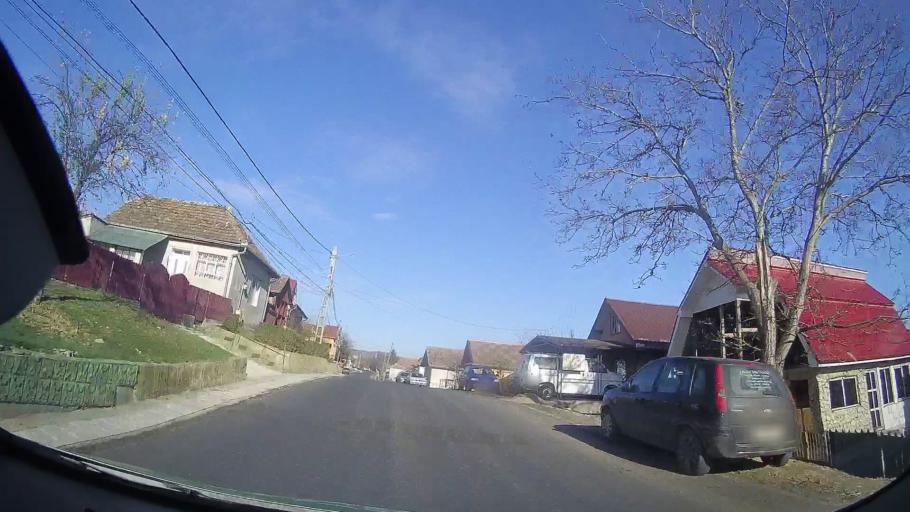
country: RO
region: Mures
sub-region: Comuna Zau De Campie
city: Zau de Campie
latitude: 46.6098
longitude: 24.1231
